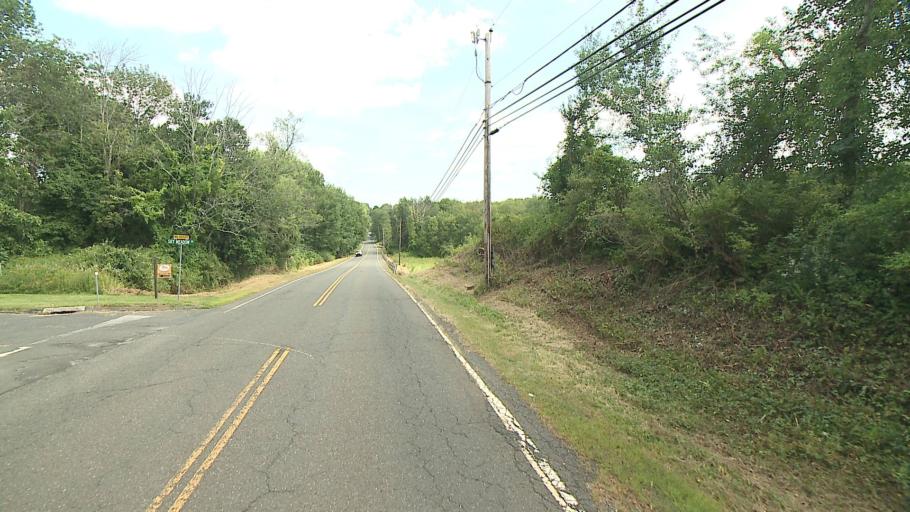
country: US
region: Connecticut
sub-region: Litchfield County
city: Bethlehem Village
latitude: 41.6494
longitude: -73.1877
